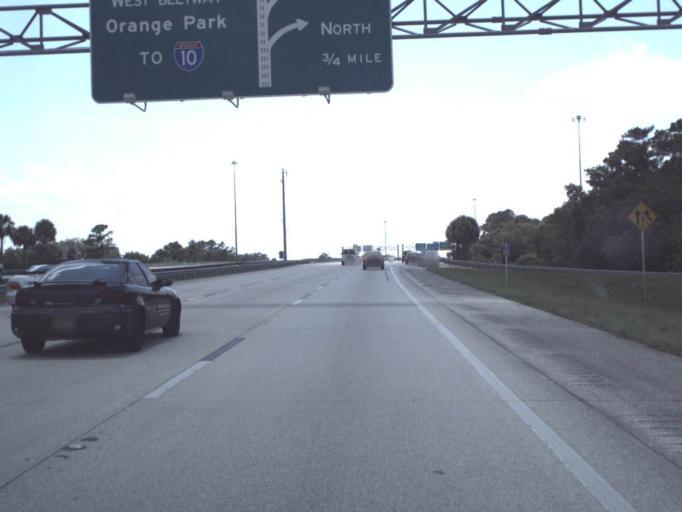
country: US
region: Florida
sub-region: Saint Johns County
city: Fruit Cove
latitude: 30.1680
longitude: -81.5386
